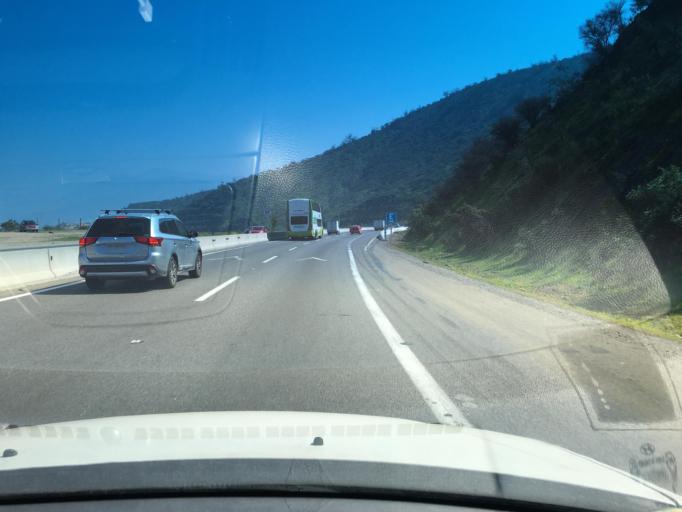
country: CL
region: Santiago Metropolitan
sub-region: Provincia de Chacabuco
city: Lampa
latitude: -33.4413
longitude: -71.0010
